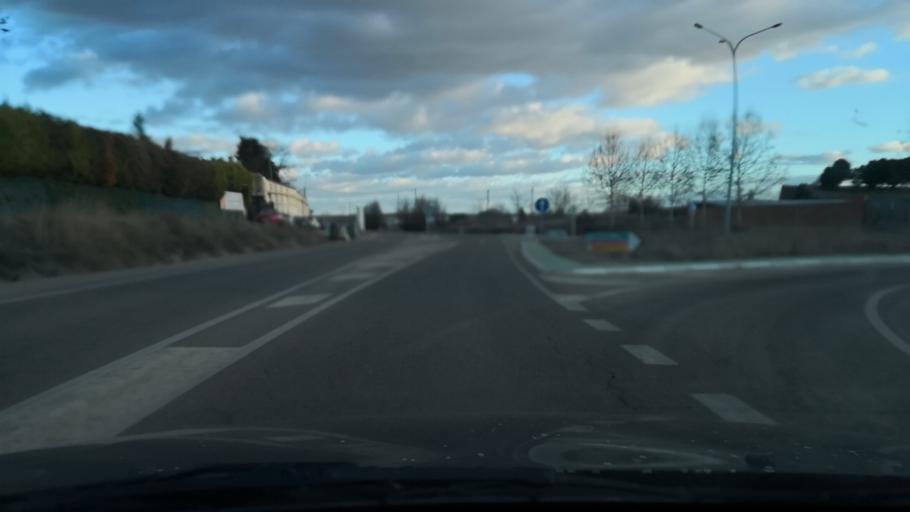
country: ES
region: Castille and Leon
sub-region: Provincia de Valladolid
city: Medina del Campo
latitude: 41.3131
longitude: -4.9056
